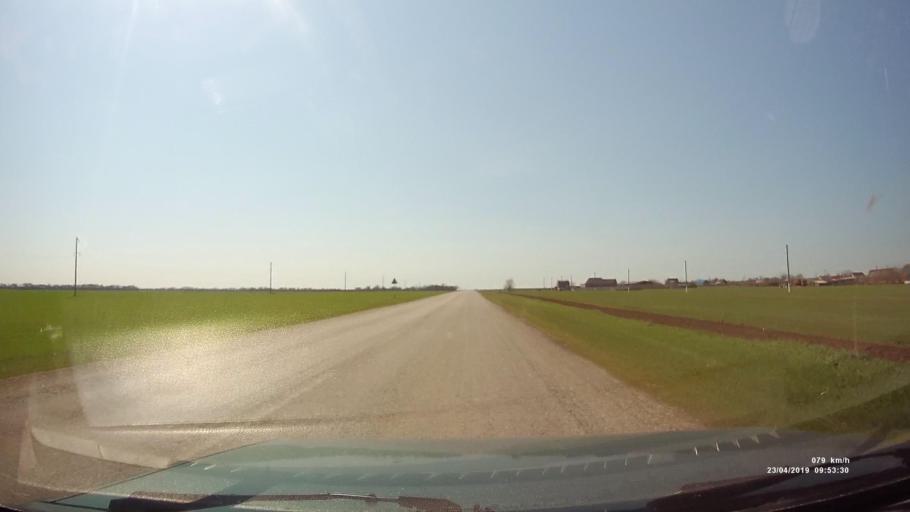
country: RU
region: Rostov
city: Orlovskiy
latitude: 46.8323
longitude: 42.0505
